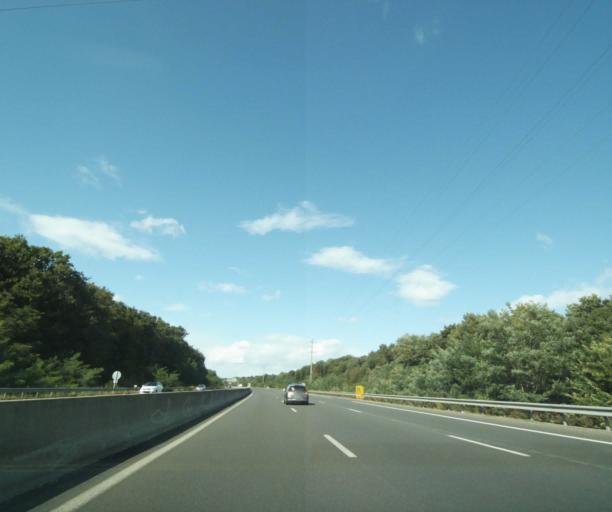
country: FR
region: Centre
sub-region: Departement du Loiret
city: Saint-Pryve-Saint-Mesmin
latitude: 47.8451
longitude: 1.8663
